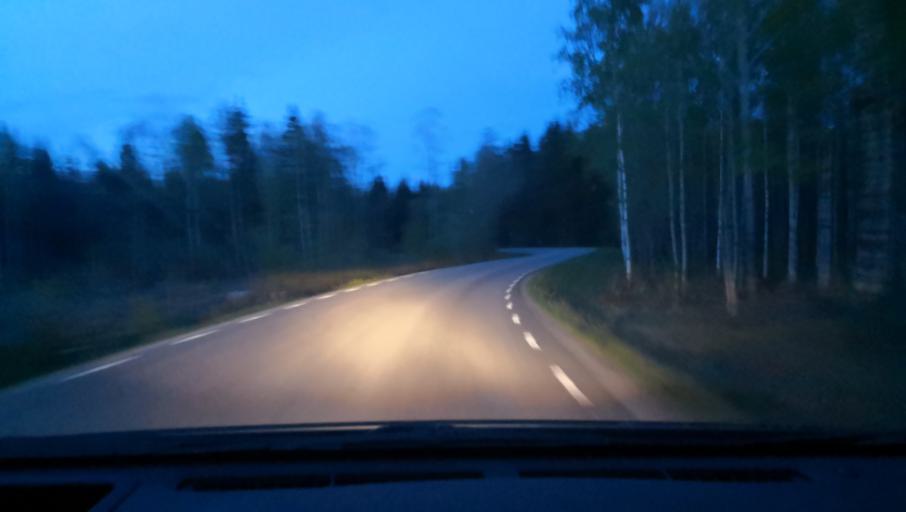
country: SE
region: OErebro
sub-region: Kumla Kommun
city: Kumla
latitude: 59.1908
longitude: 15.0528
